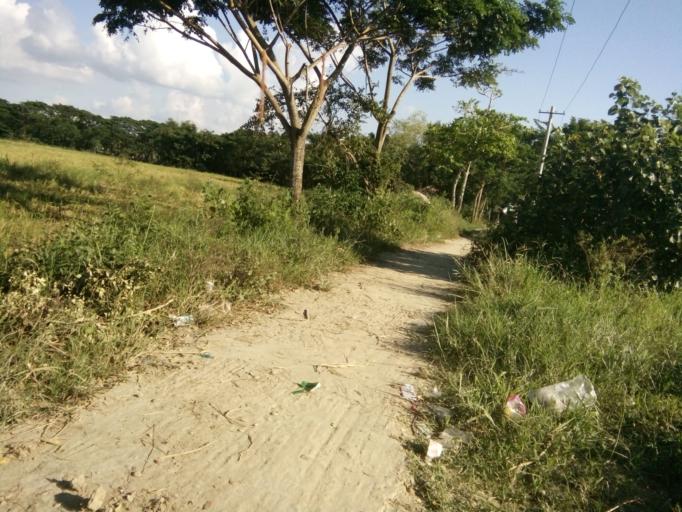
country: MM
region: Yangon
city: Kanbe
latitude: 16.8755
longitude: 95.9774
